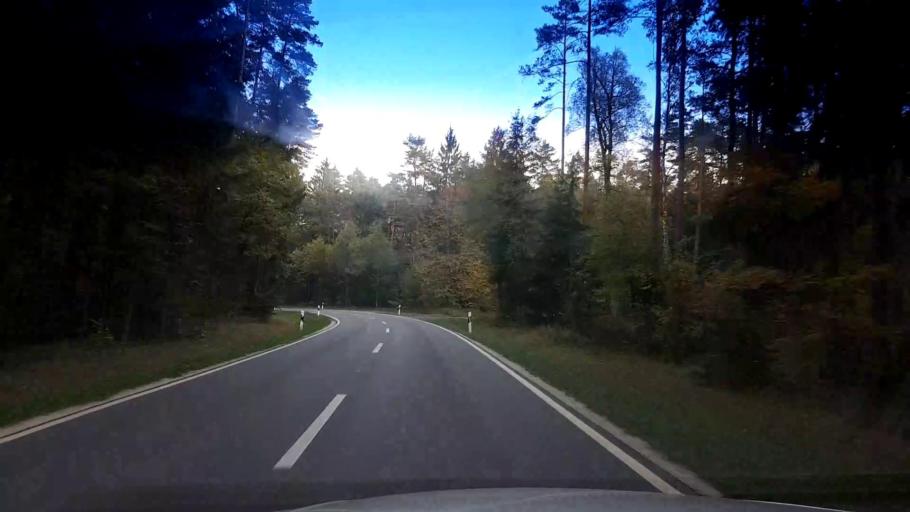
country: DE
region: Bavaria
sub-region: Upper Franconia
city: Weismain
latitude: 50.0965
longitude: 11.2546
